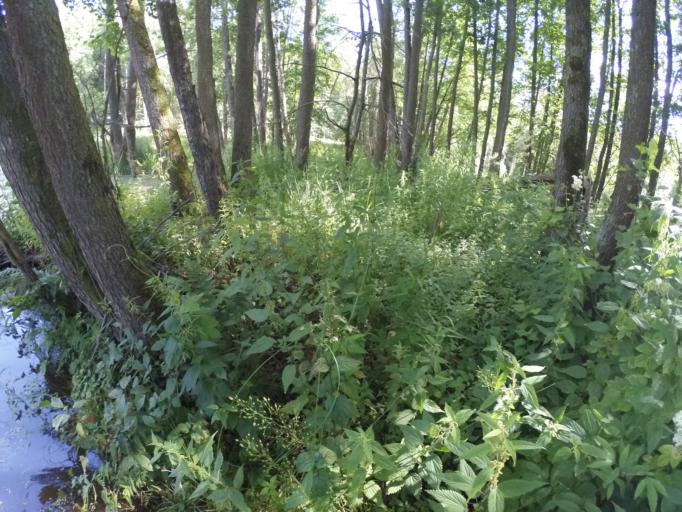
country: RU
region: Moskovskaya
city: Fosforitnyy
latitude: 55.3394
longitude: 38.9381
